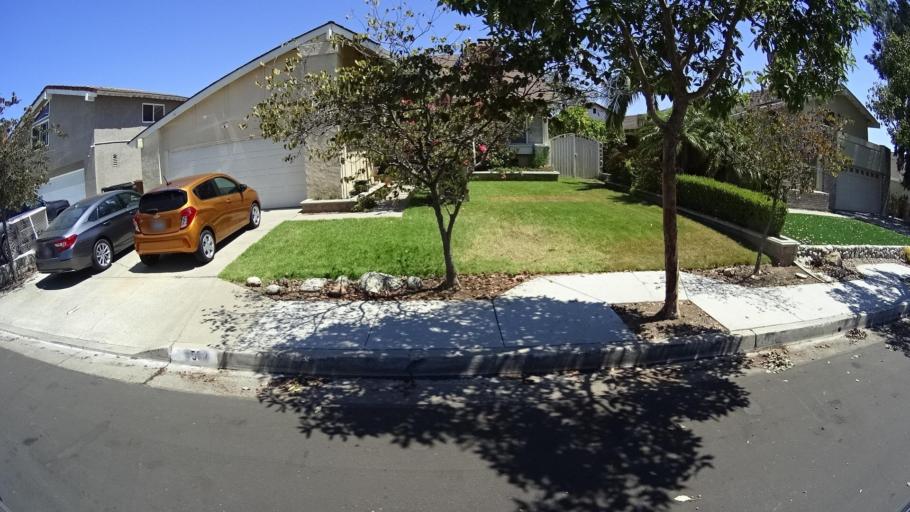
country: US
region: California
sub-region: Orange County
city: Yorba Linda
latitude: 33.8803
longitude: -117.7914
